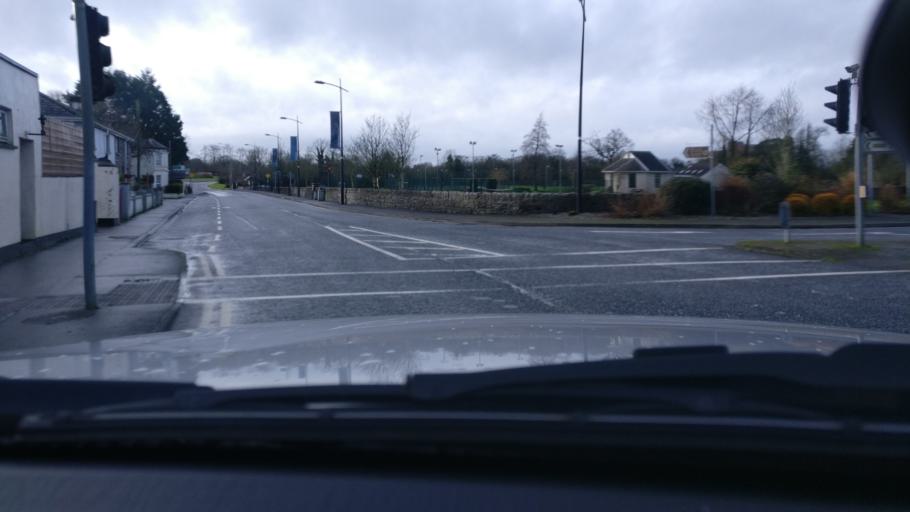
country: IE
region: Leinster
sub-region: An Longfort
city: Edgeworthstown
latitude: 53.6968
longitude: -7.6120
